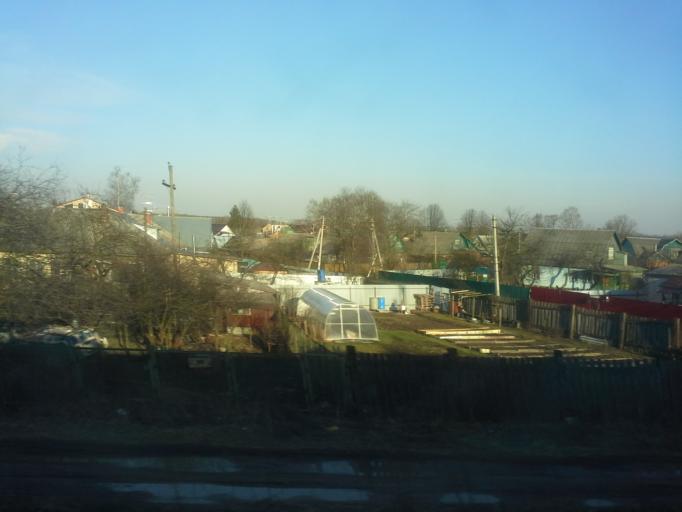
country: RU
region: Moskovskaya
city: Nekrasovskiy
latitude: 56.0947
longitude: 37.5064
